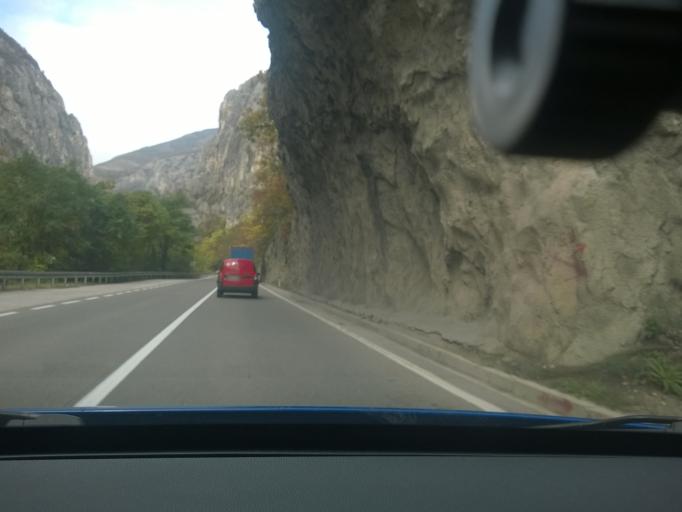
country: RS
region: Central Serbia
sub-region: Nisavski Okrug
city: Svrljig
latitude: 43.3244
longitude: 22.1651
